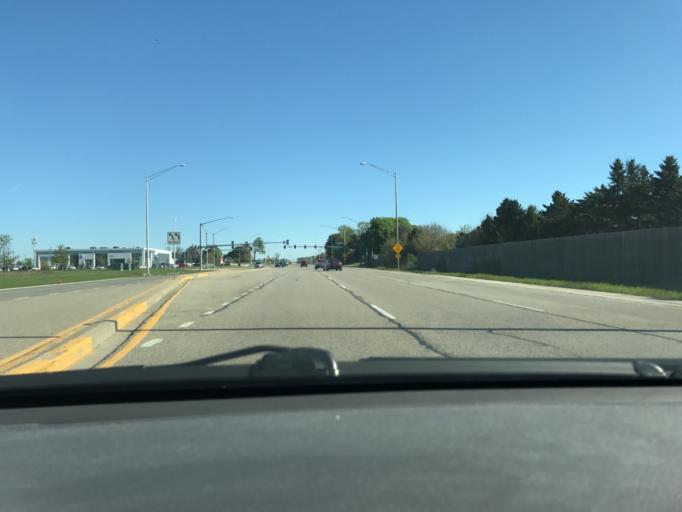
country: US
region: Illinois
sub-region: Kane County
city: Sleepy Hollow
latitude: 42.0839
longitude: -88.3354
